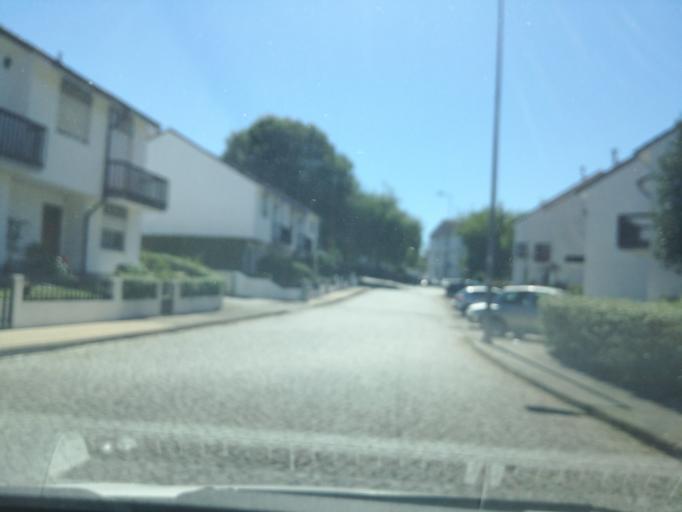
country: PT
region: Porto
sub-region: Maia
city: Maia
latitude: 41.2437
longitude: -8.6175
